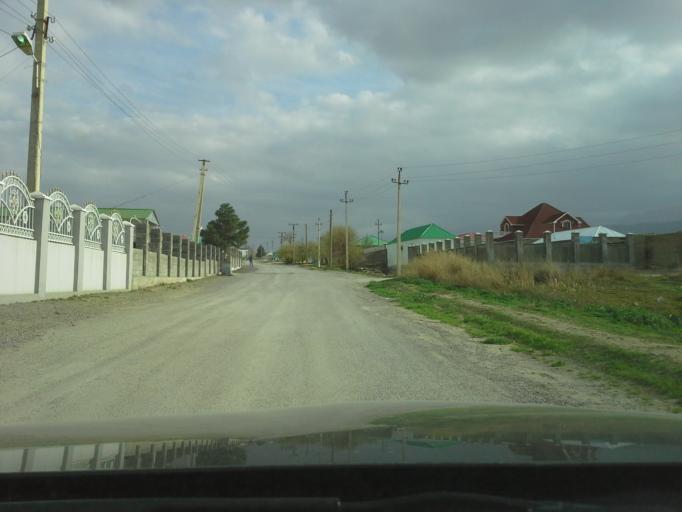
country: TM
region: Ahal
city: Abadan
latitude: 37.9645
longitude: 58.2298
